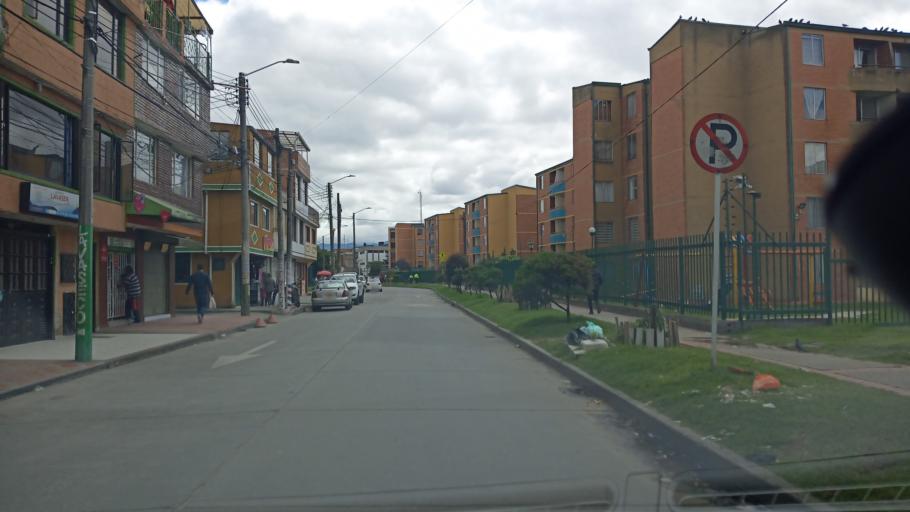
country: CO
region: Cundinamarca
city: Funza
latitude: 4.6693
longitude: -74.1498
